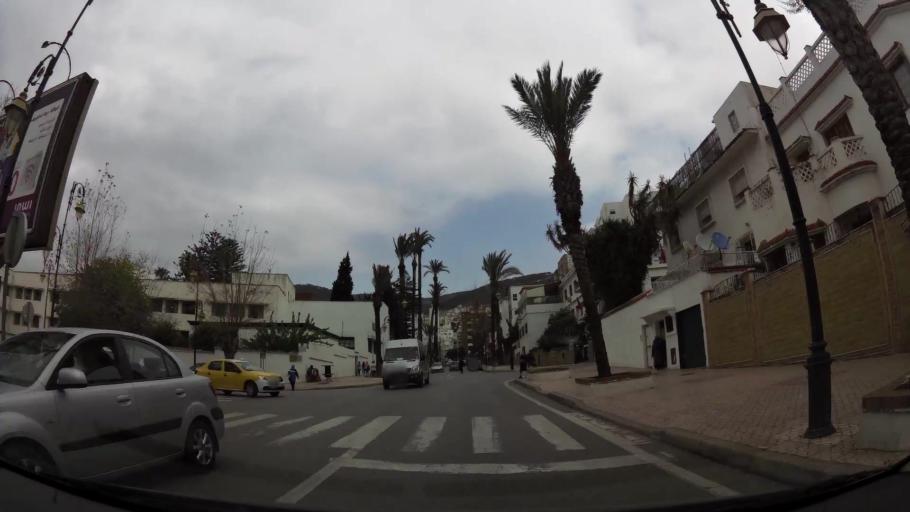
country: MA
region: Tanger-Tetouan
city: Tetouan
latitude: 35.5718
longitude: -5.3797
